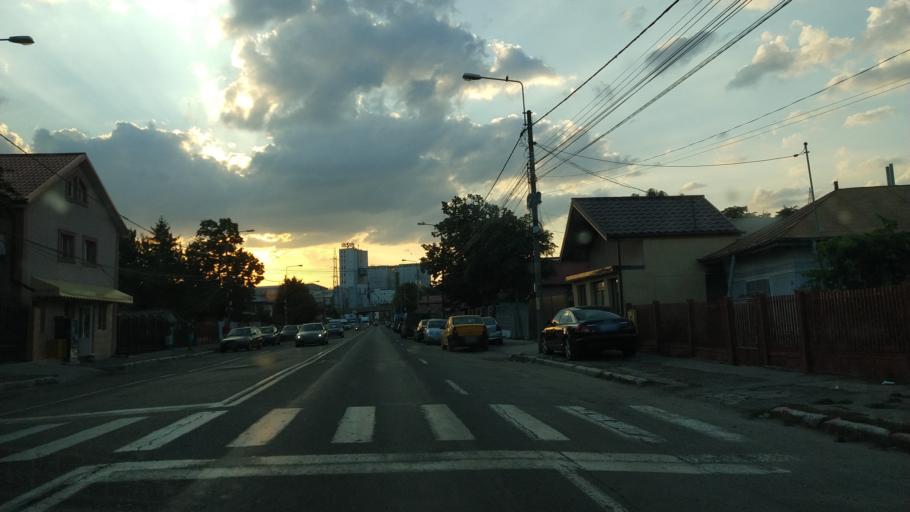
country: RO
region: Buzau
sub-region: Comuna Maracineni
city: Potoceni
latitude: 45.1621
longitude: 26.7925
